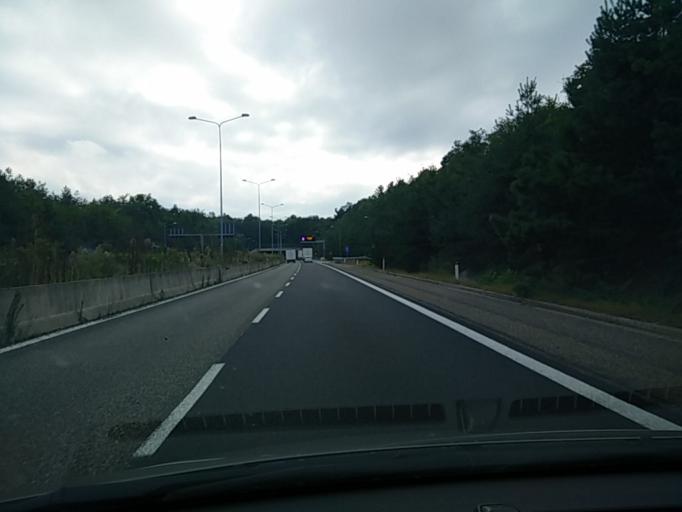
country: IT
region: Lombardy
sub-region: Provincia di Varese
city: Vizzola Ticino
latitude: 45.6445
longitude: 8.7048
